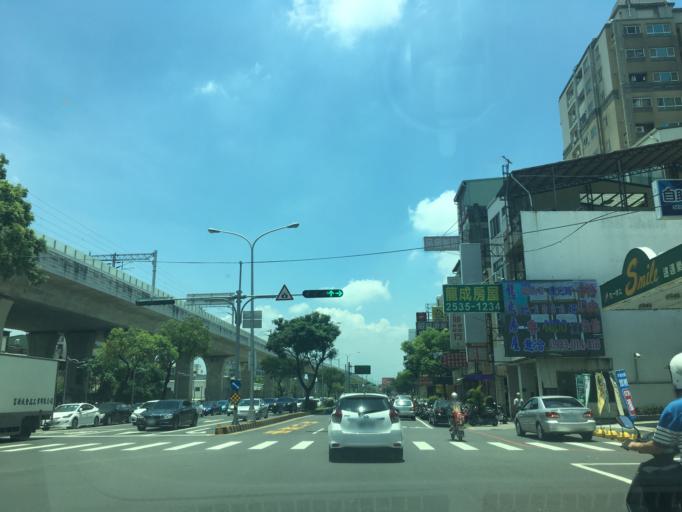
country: TW
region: Taiwan
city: Fengyuan
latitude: 24.2117
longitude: 120.7053
